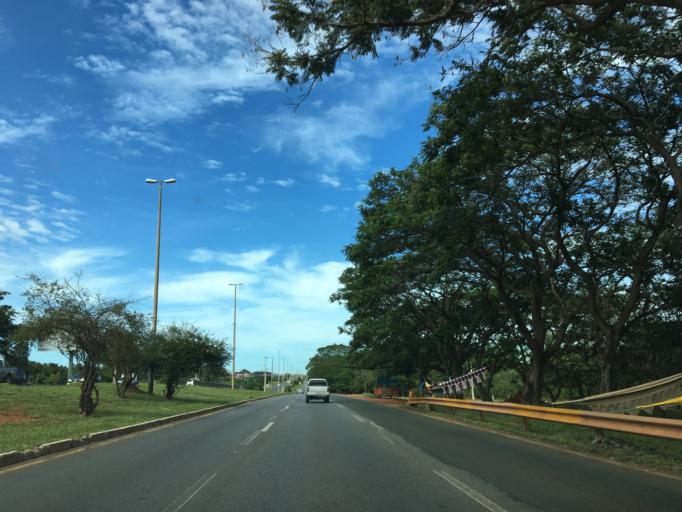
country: BR
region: Federal District
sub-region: Brasilia
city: Brasilia
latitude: -15.8661
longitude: -47.9430
